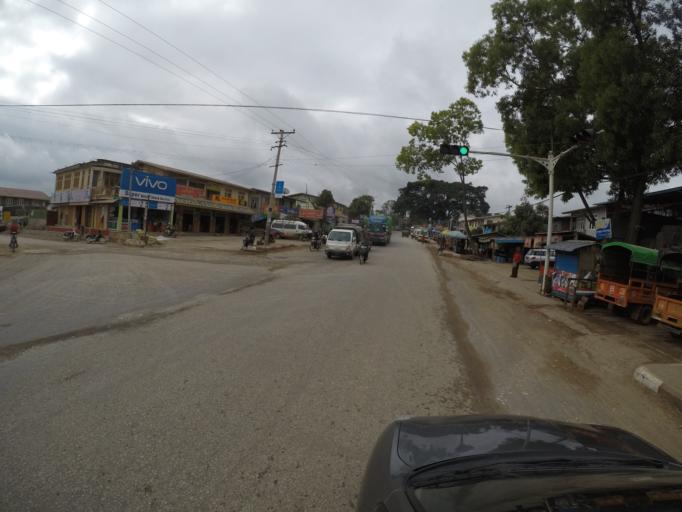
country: MM
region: Shan
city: Taunggyi
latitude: 20.6548
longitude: 96.6290
